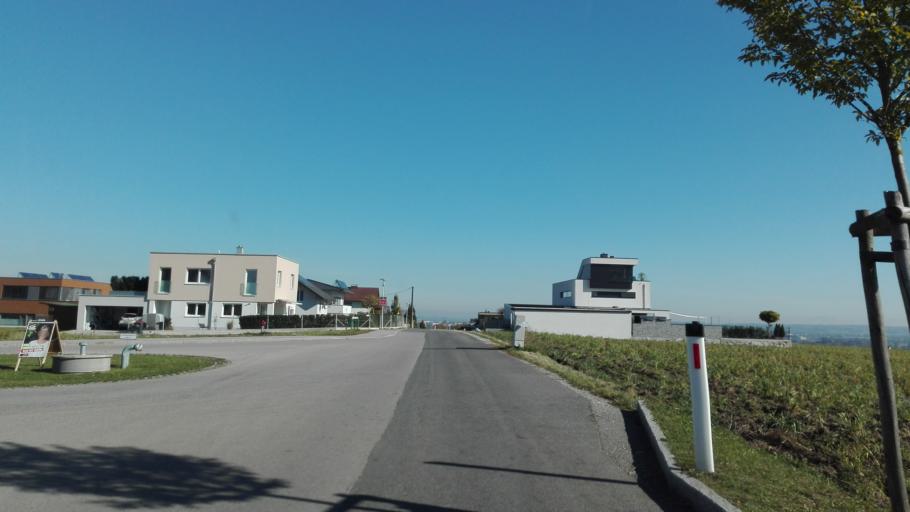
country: AT
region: Upper Austria
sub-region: Politischer Bezirk Linz-Land
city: Pasching
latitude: 48.2670
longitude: 14.1833
